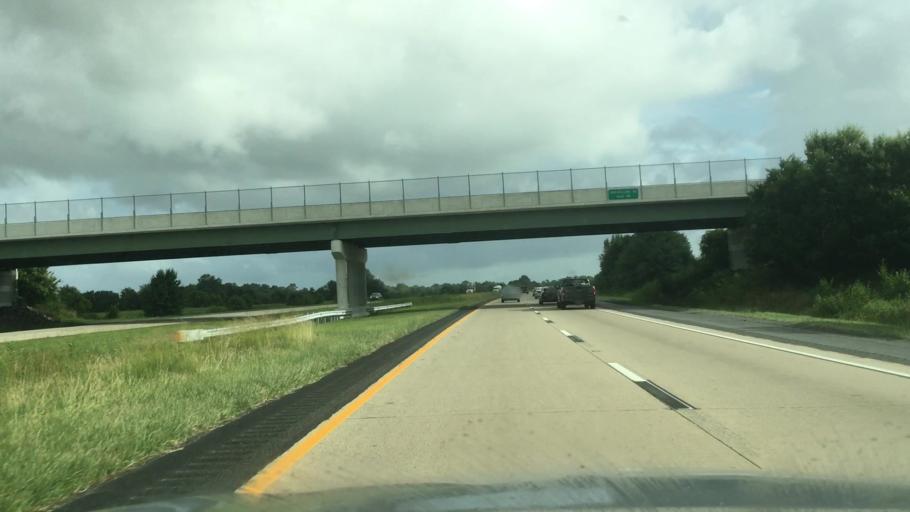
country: US
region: Delaware
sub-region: Kent County
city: Cheswold
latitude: 39.2544
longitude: -75.5789
